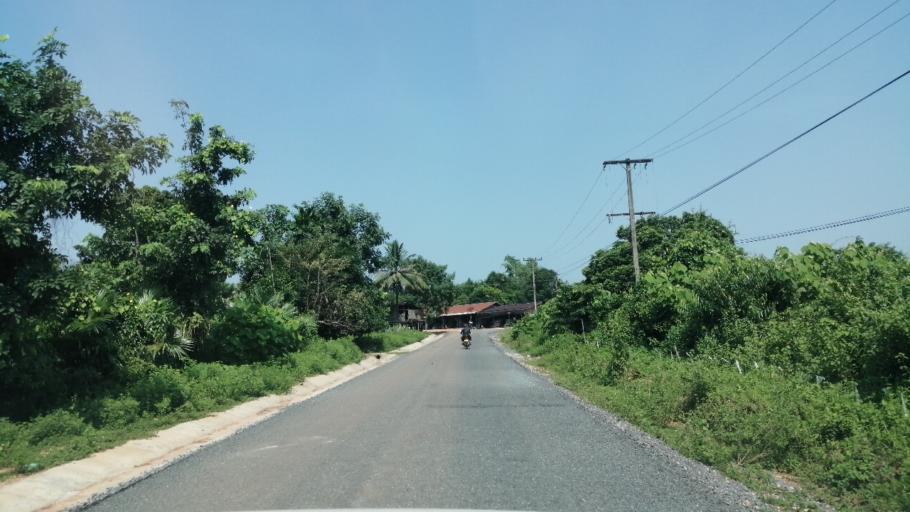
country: LA
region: Bolikhamxai
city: Bolikhan
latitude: 18.4606
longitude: 103.7965
